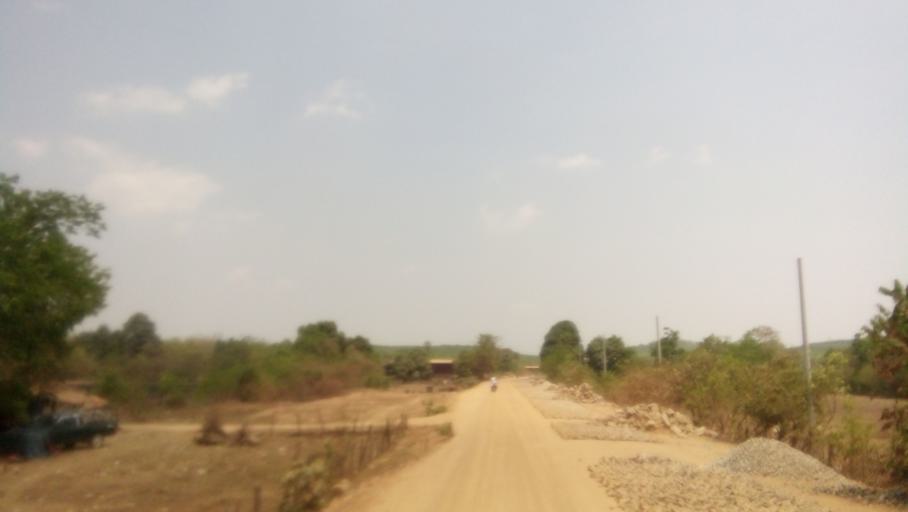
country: MM
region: Kayin
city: Hpa-an
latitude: 17.1582
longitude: 97.8021
